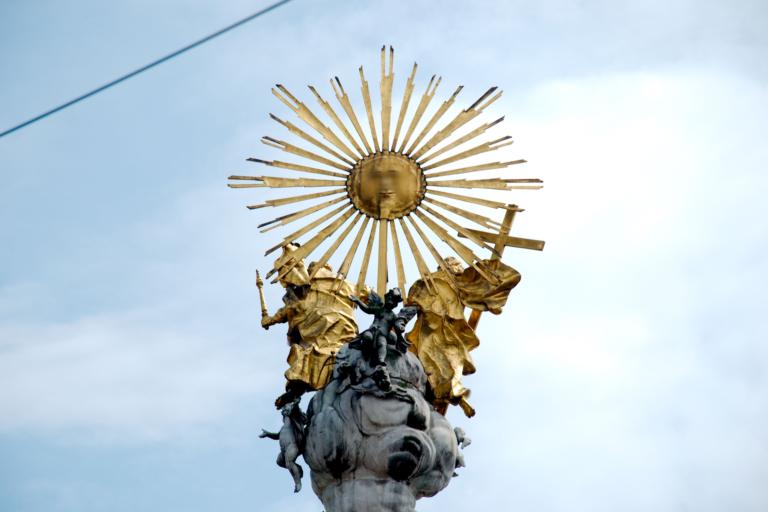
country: AT
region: Upper Austria
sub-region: Linz Stadt
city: Linz
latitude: 48.3061
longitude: 14.2862
